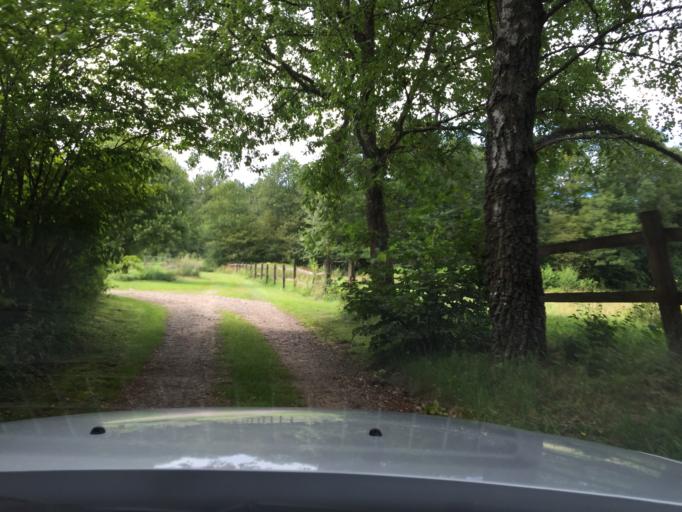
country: SE
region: Skane
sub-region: Hassleholms Kommun
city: Sosdala
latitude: 56.0086
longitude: 13.6350
